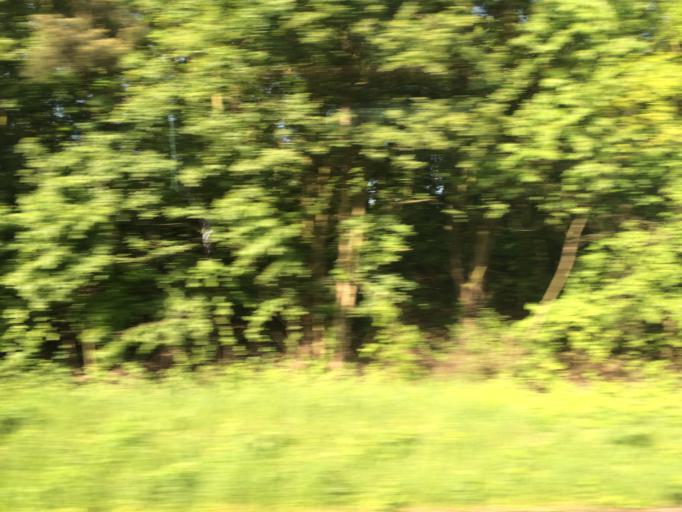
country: DE
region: North Rhine-Westphalia
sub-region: Regierungsbezirk Koln
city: Konigswinter
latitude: 50.7222
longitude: 7.1511
